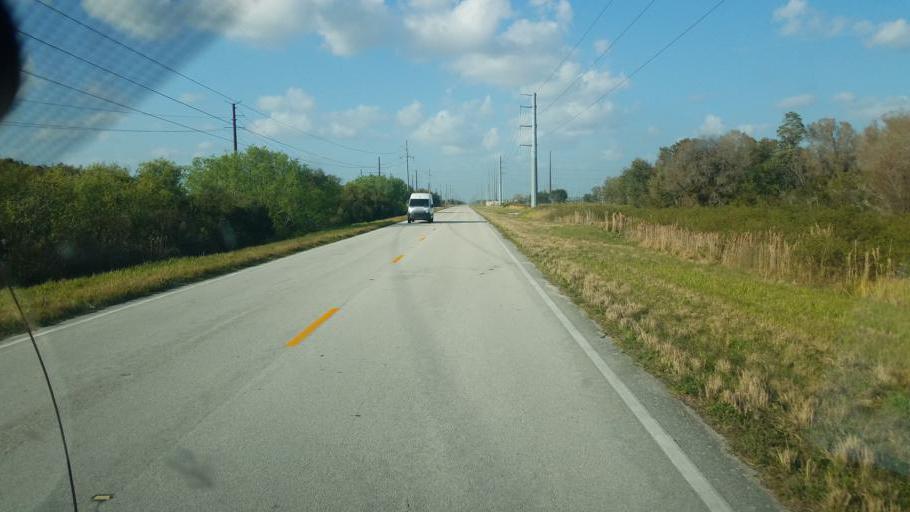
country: US
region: Florida
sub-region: Hardee County
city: Wauchula
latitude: 27.5182
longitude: -81.9258
